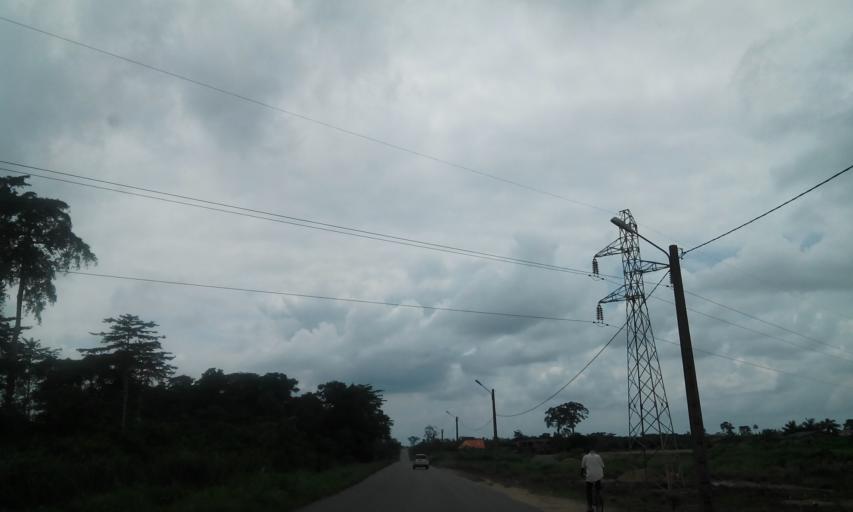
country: CI
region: Sud-Comoe
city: Aboisso
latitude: 5.4298
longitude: -3.2645
